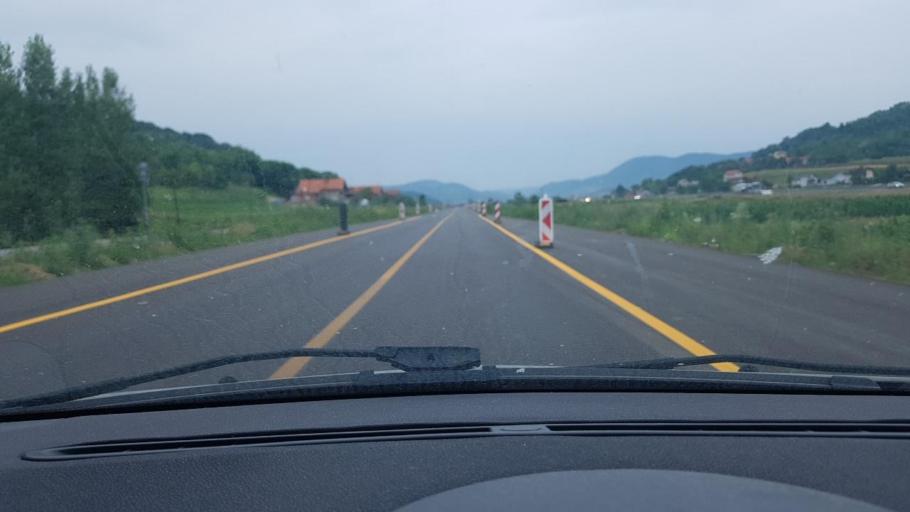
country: HR
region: Krapinsko-Zagorska
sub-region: Grad Krapina
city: Krapina
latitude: 46.1024
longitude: 15.8958
